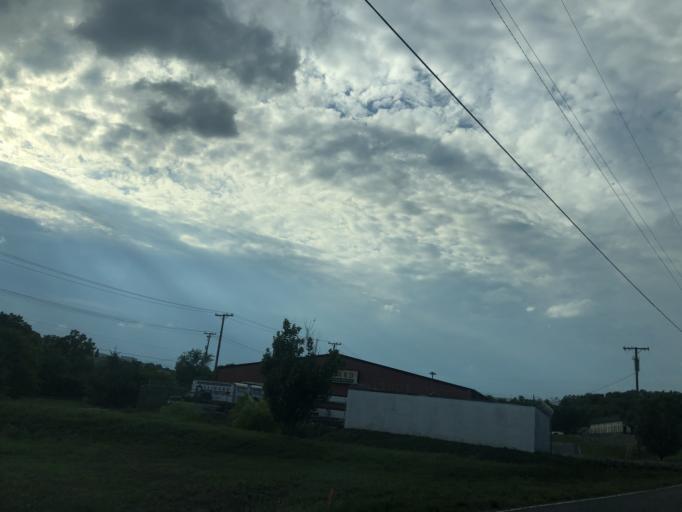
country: US
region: Tennessee
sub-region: Davidson County
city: Nashville
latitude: 36.2131
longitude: -86.7784
